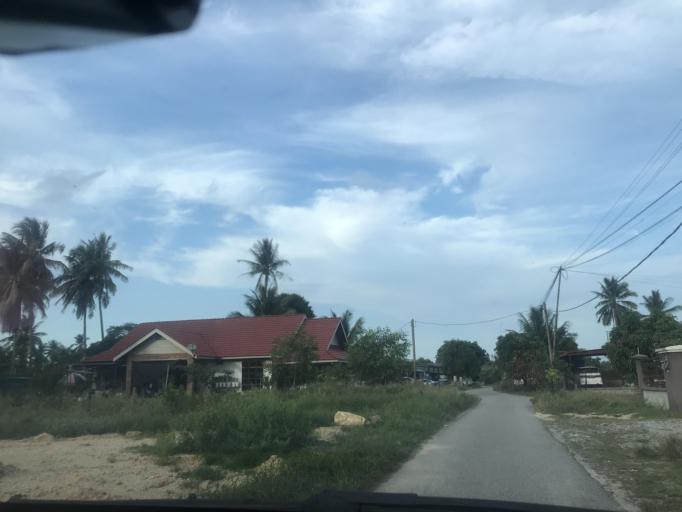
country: MY
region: Kelantan
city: Peringat
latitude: 6.1194
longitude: 102.3557
